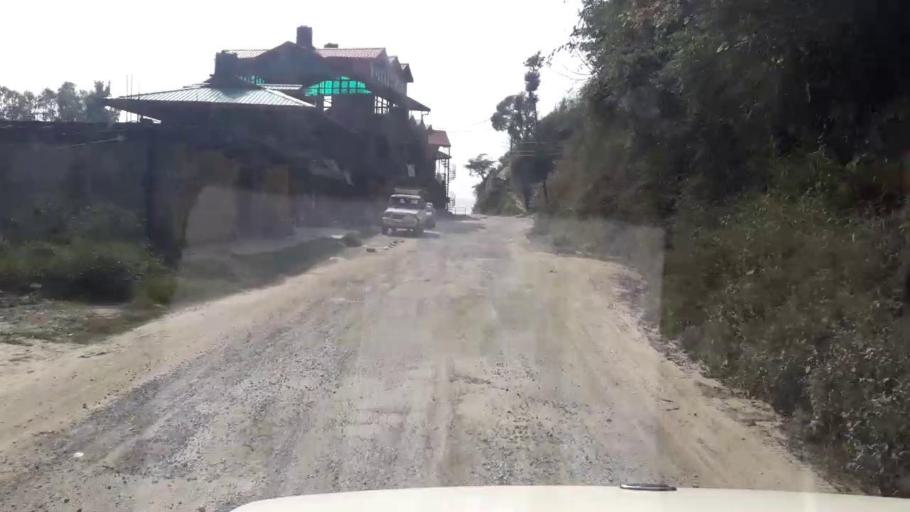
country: IN
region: Himachal Pradesh
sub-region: Shimla
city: Shimla
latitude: 31.0477
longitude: 77.1504
